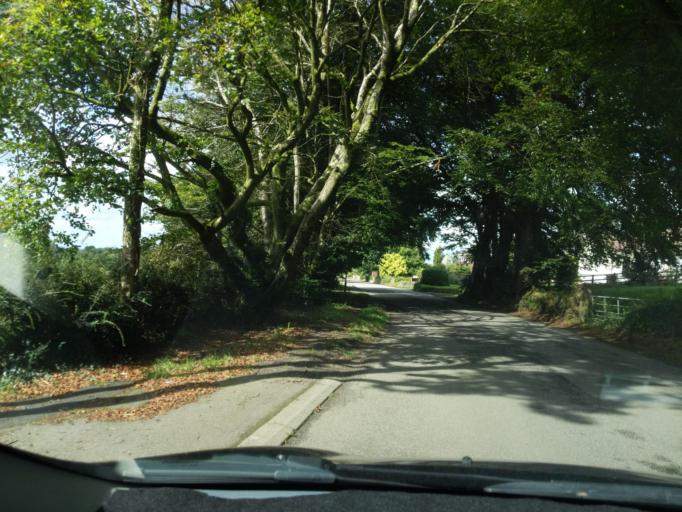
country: GB
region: England
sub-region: Cornwall
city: Callington
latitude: 50.5172
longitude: -4.3123
